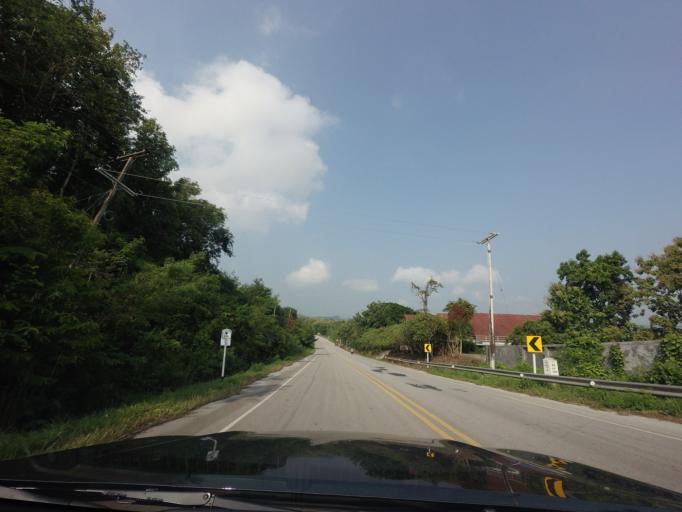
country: TH
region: Loei
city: Chiang Khan
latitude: 17.8898
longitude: 101.6254
